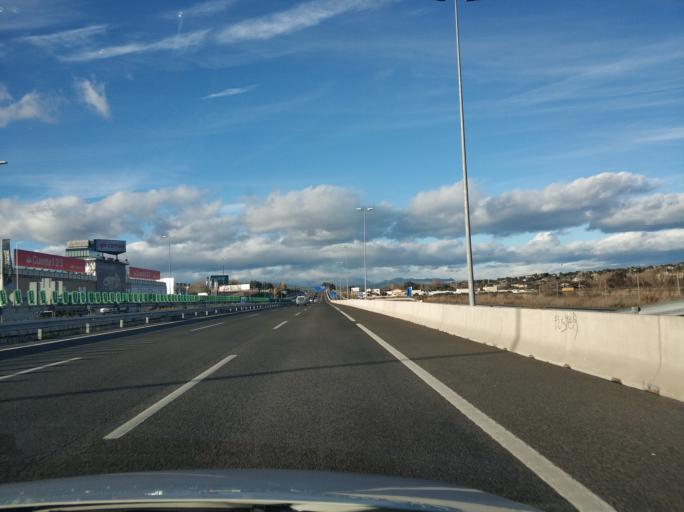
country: ES
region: Madrid
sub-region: Provincia de Madrid
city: San Agustin de Guadalix
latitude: 40.6152
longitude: -3.5822
